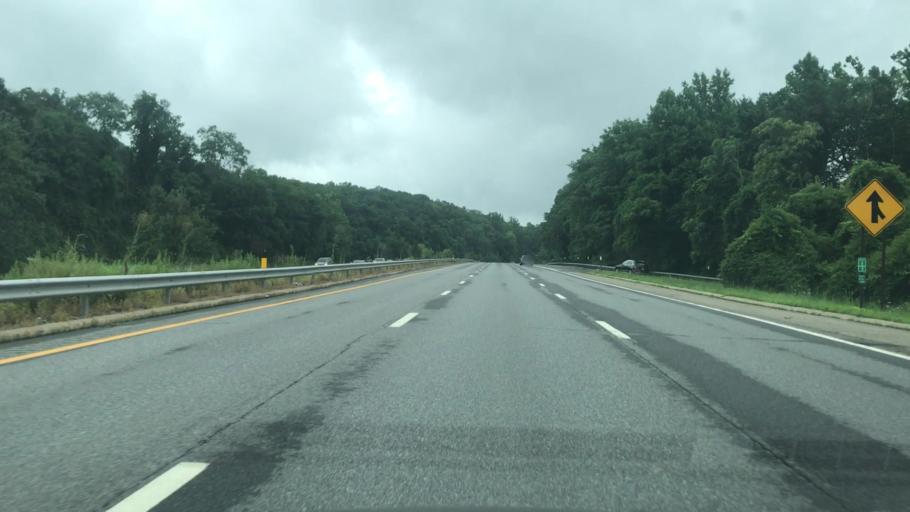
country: US
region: New York
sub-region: Westchester County
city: Briarcliff Manor
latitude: 41.1831
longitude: -73.8075
